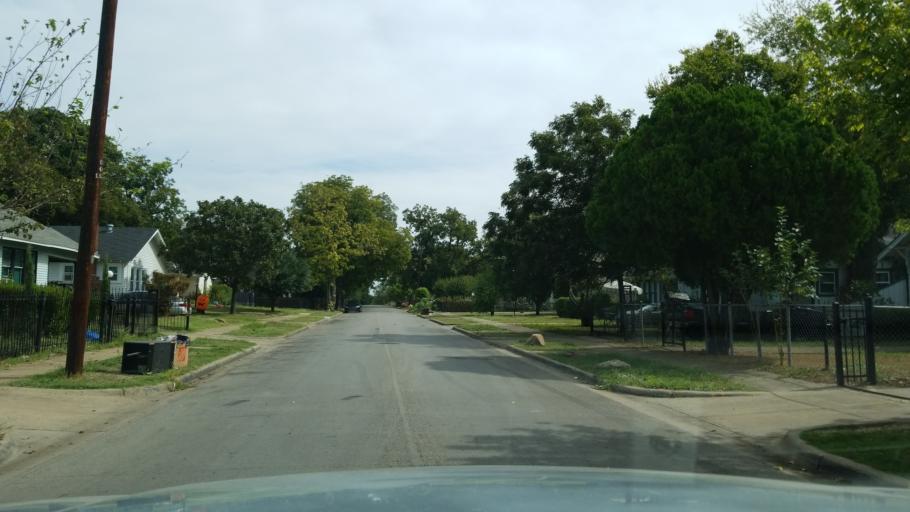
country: US
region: Texas
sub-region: Dallas County
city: Dallas
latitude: 32.7873
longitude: -96.7398
